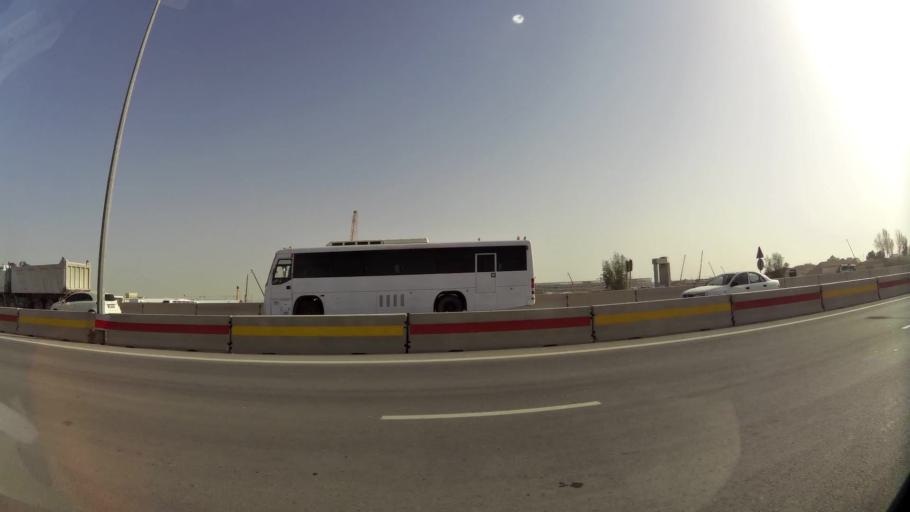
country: QA
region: Baladiyat ar Rayyan
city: Ar Rayyan
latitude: 25.3190
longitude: 51.4251
